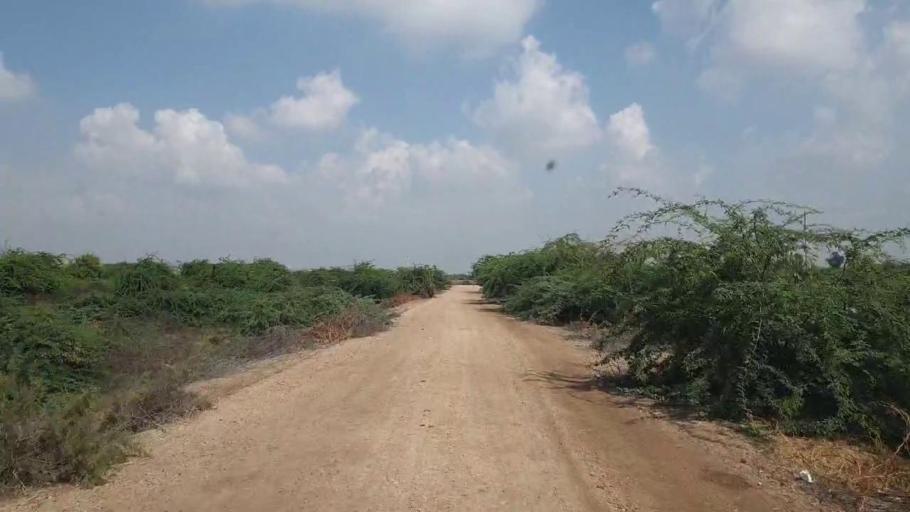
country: PK
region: Sindh
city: Badin
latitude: 24.4924
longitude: 68.6550
